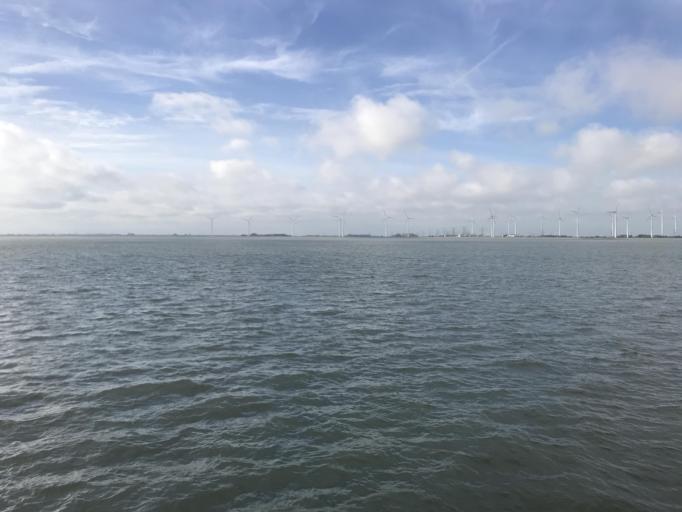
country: NL
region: Groningen
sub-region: Gemeente Delfzijl
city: Delfzijl
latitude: 53.4333
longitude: 6.9133
